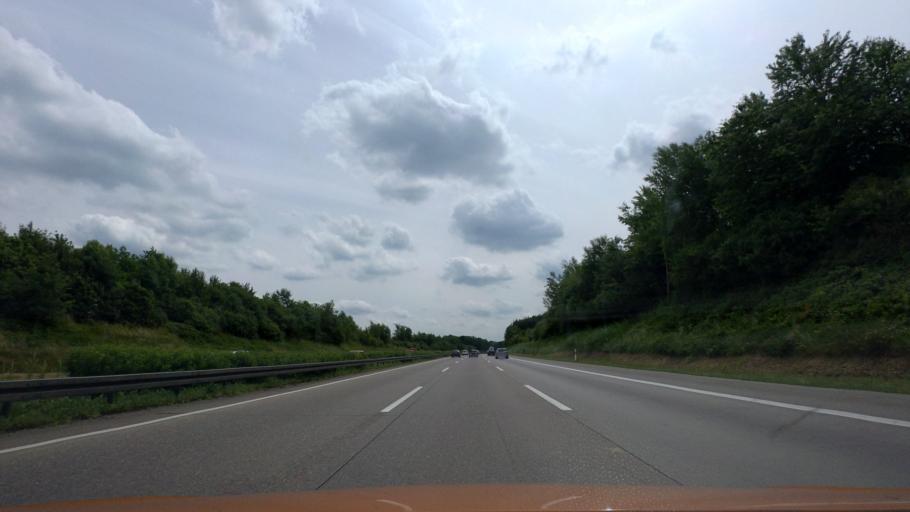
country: DE
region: Lower Saxony
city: Isernhagen Farster Bauerschaft
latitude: 52.4709
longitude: 9.8561
